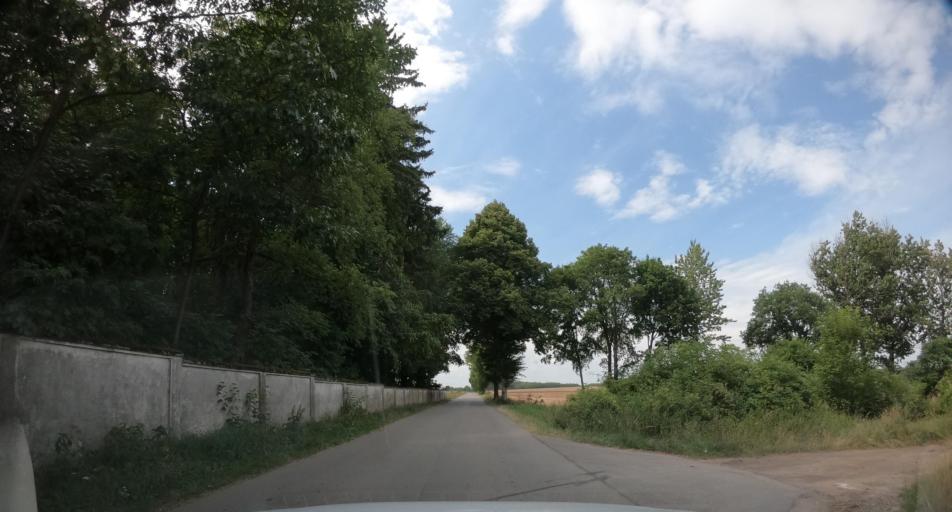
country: PL
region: West Pomeranian Voivodeship
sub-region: Powiat walecki
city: Tuczno
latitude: 53.2350
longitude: 16.1583
